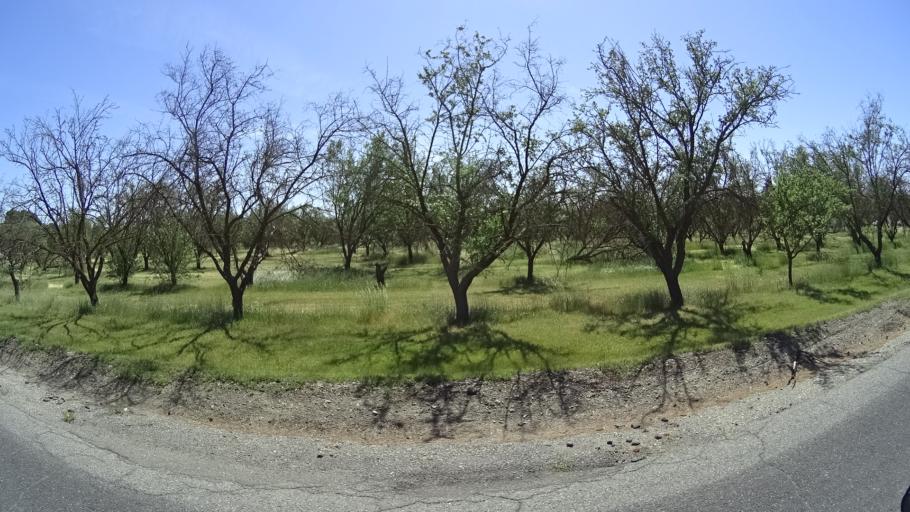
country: US
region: California
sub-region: Glenn County
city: Orland
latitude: 39.7325
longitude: -122.1518
